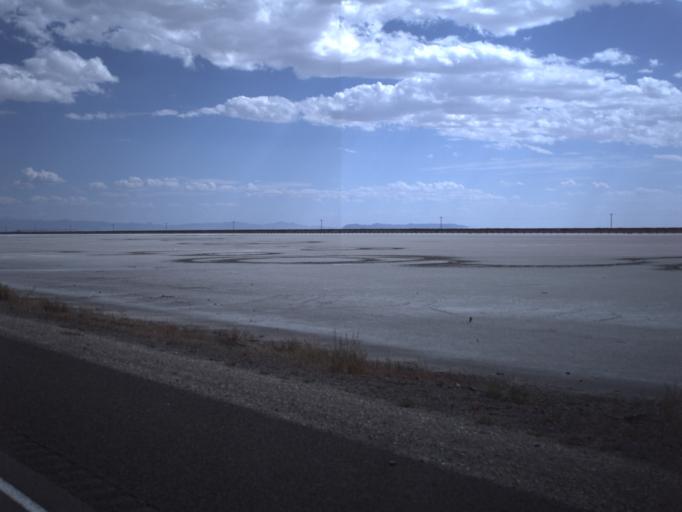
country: US
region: Utah
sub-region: Tooele County
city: Wendover
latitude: 40.7350
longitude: -113.6816
